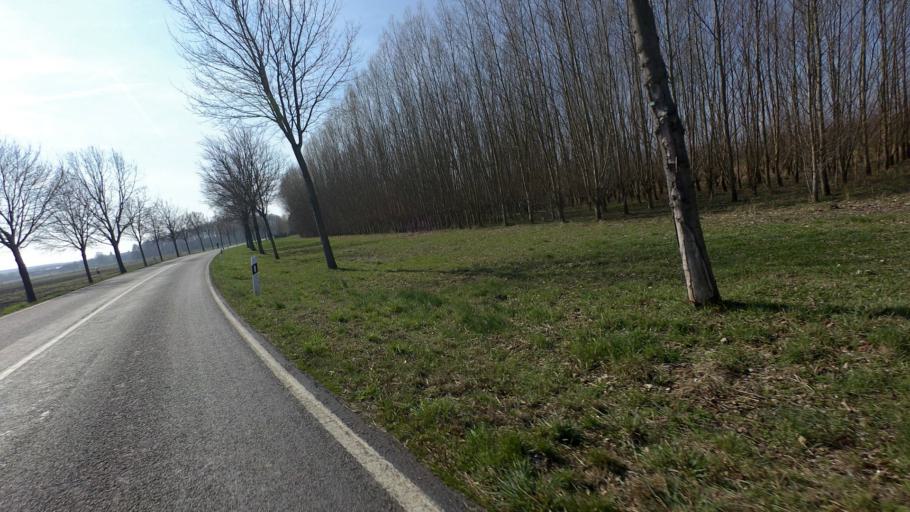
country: DE
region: Brandenburg
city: Sperenberg
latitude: 52.0561
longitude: 13.3244
